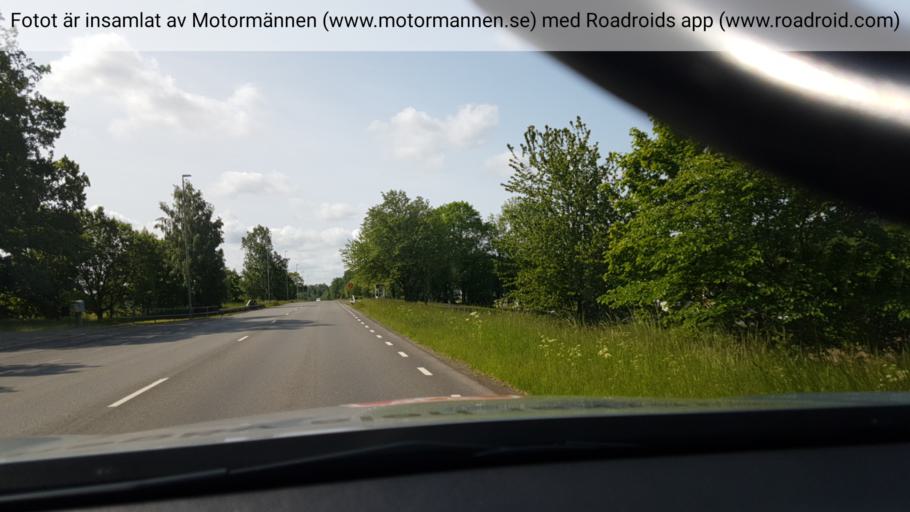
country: SE
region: Vaestra Goetaland
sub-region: Skovde Kommun
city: Skoevde
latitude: 58.4194
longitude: 13.8459
